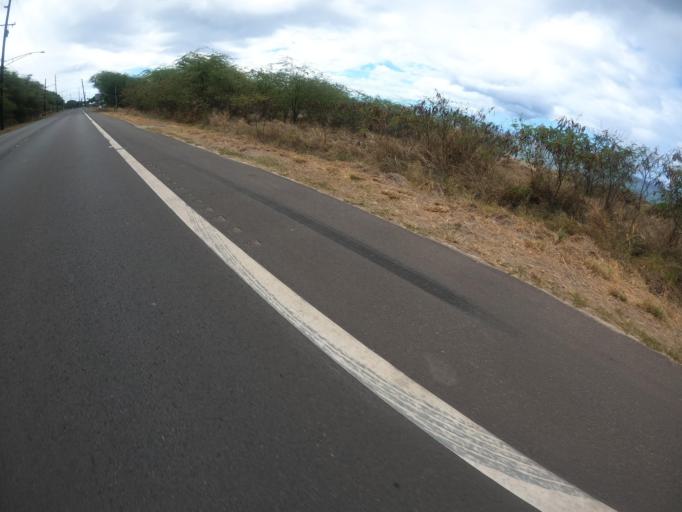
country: US
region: Hawaii
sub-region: Honolulu County
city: Makaha
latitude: 21.4895
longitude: -158.2292
